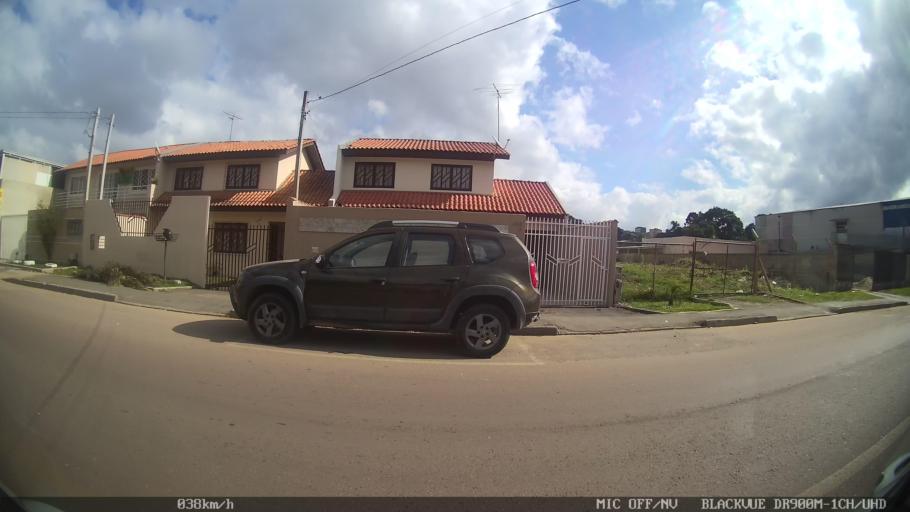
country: BR
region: Parana
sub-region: Colombo
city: Colombo
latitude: -25.3651
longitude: -49.1958
